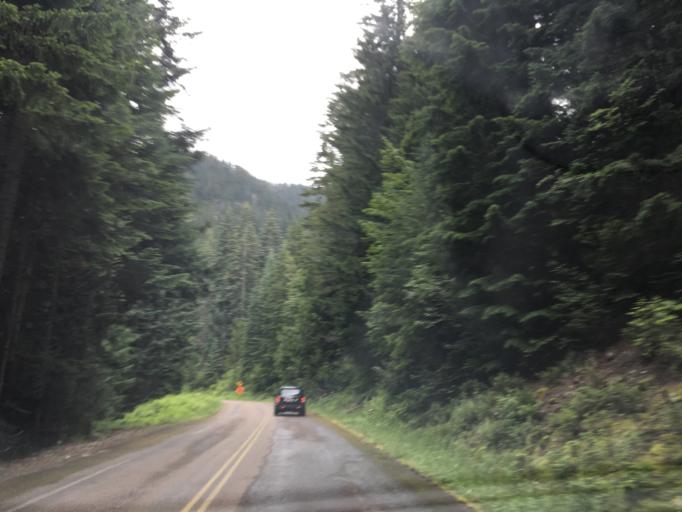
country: US
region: Washington
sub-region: Chelan County
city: Leavenworth
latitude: 47.7516
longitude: -121.1260
